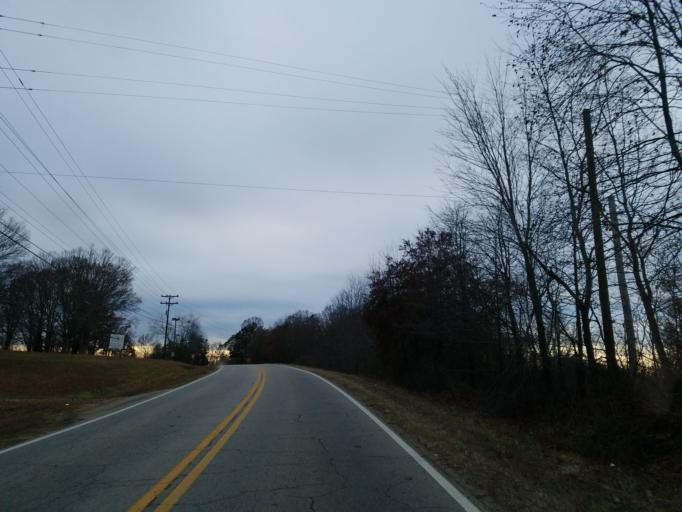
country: US
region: Georgia
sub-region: Dawson County
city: Dawsonville
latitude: 34.3829
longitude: -84.0183
